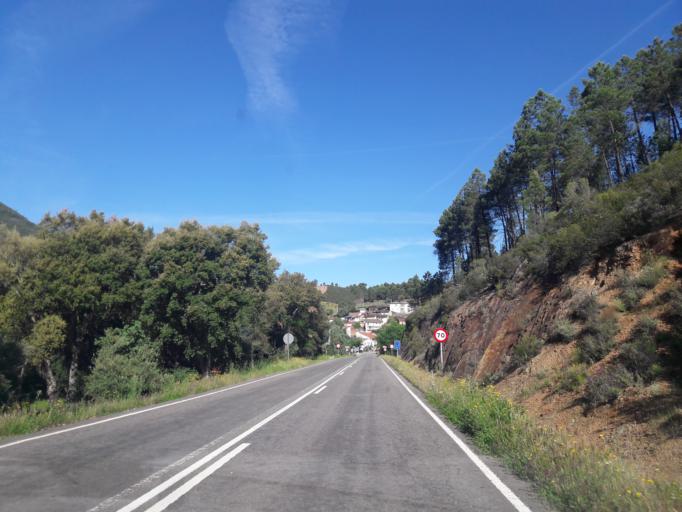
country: ES
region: Castille and Leon
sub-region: Provincia de Salamanca
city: Herguijuela de la Sierra
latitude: 40.4037
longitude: -6.0815
